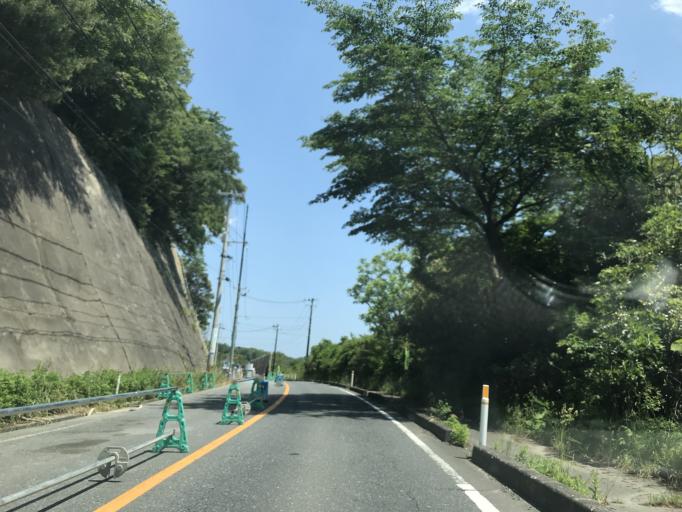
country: JP
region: Miyagi
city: Matsushima
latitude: 38.3805
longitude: 141.1236
